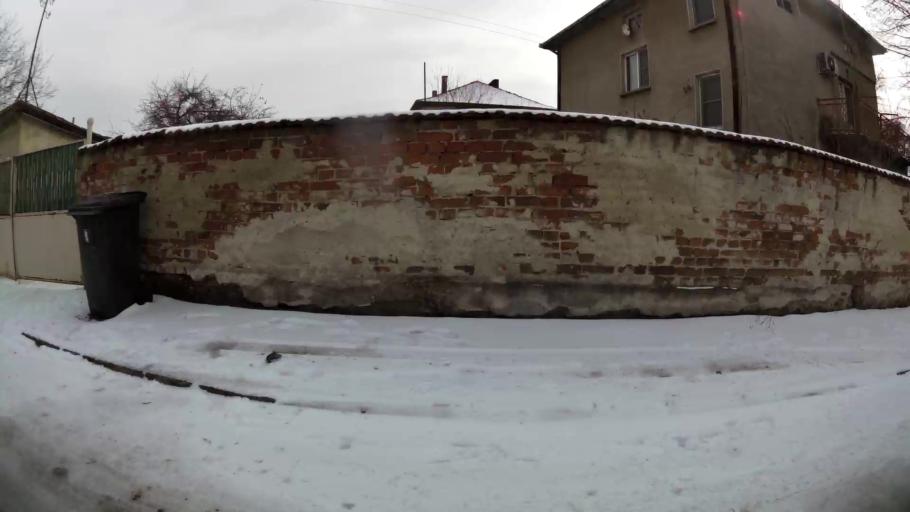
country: BG
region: Sofia-Capital
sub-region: Stolichna Obshtina
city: Sofia
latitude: 42.7132
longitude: 23.4091
